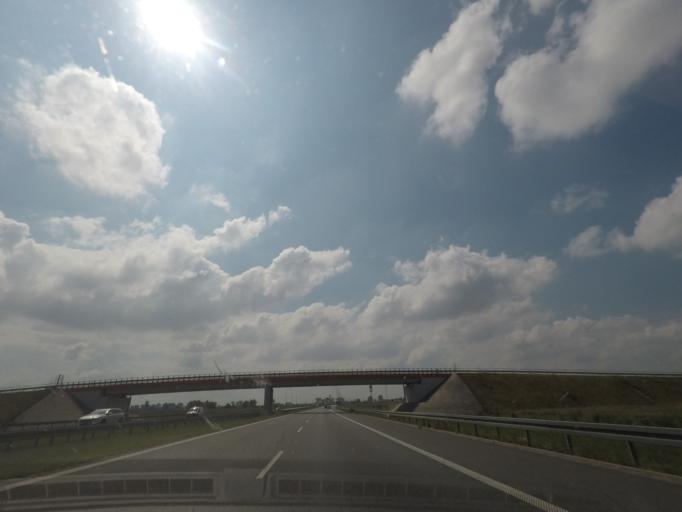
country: PL
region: Lodz Voivodeship
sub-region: Powiat kutnowski
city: Krzyzanow
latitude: 52.1929
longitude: 19.4868
